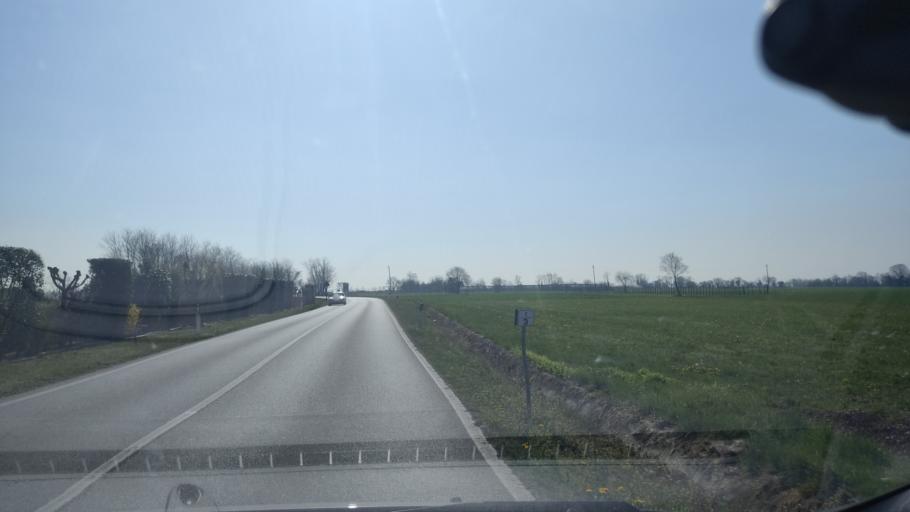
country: IT
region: Friuli Venezia Giulia
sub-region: Provincia di Pordenone
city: Budoia
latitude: 46.0285
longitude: 12.5571
